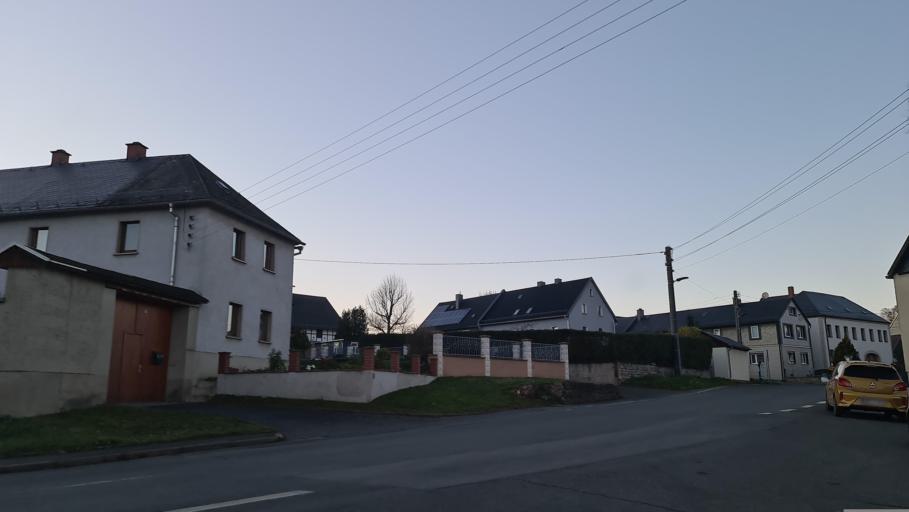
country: DE
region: Thuringia
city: Dittersdorf
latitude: 50.6429
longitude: 11.8167
